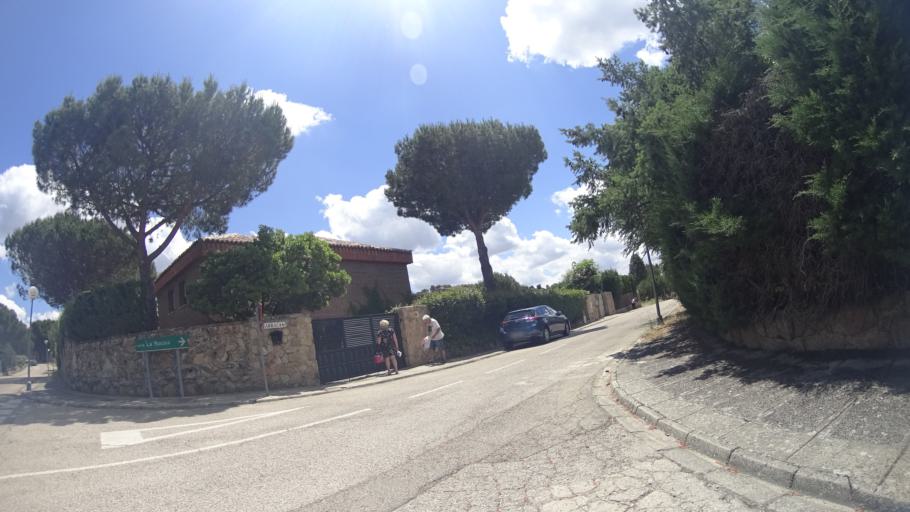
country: ES
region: Madrid
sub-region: Provincia de Madrid
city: Hoyo de Manzanares
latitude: 40.6119
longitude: -3.9322
